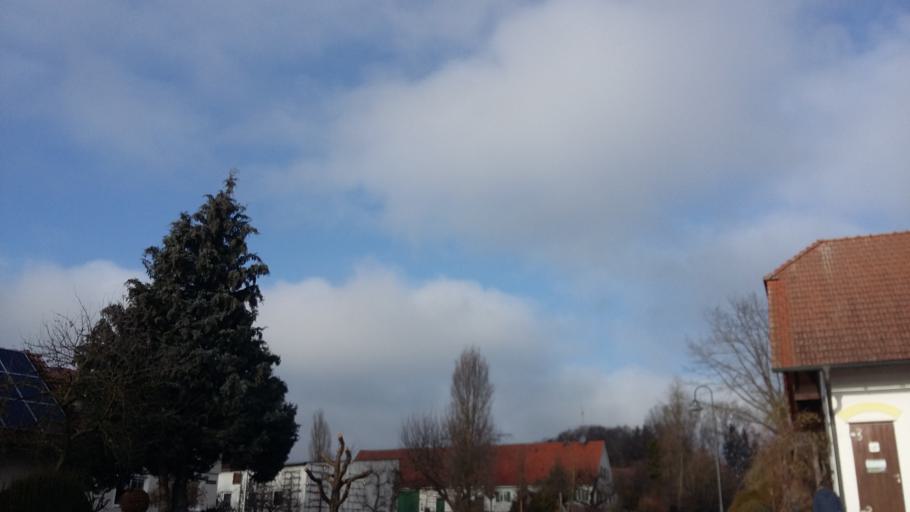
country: DE
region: Bavaria
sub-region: Swabia
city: Sielenbach
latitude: 48.4046
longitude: 11.1647
